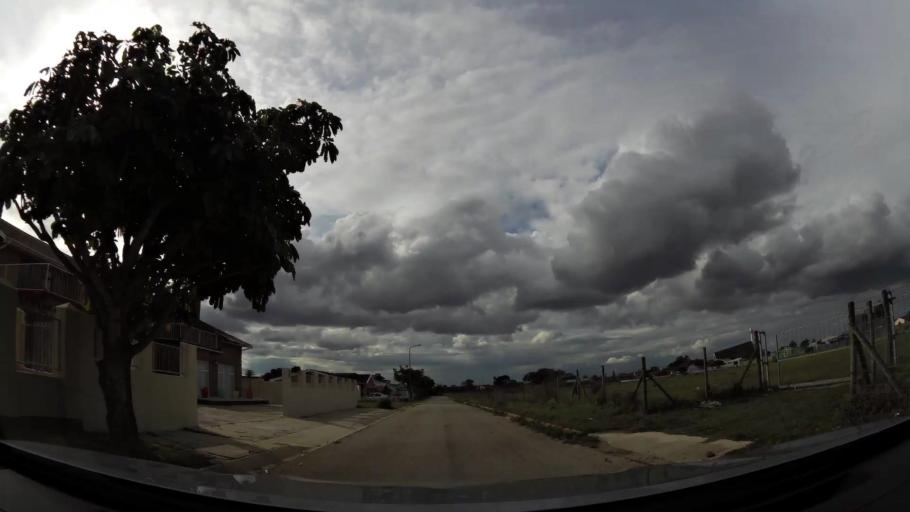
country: ZA
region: Eastern Cape
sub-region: Nelson Mandela Bay Metropolitan Municipality
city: Port Elizabeth
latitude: -33.9393
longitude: 25.5062
